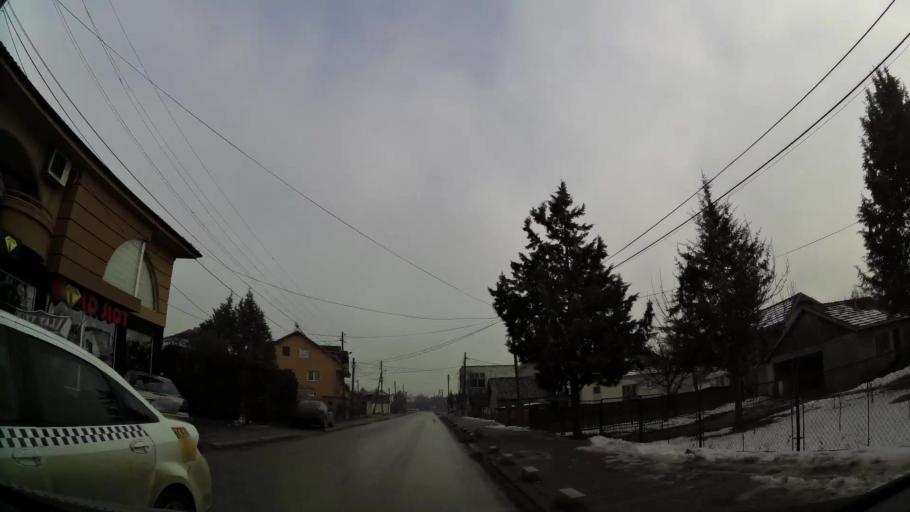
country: MK
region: Ilinden
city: Ilinden
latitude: 41.9950
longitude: 21.5718
